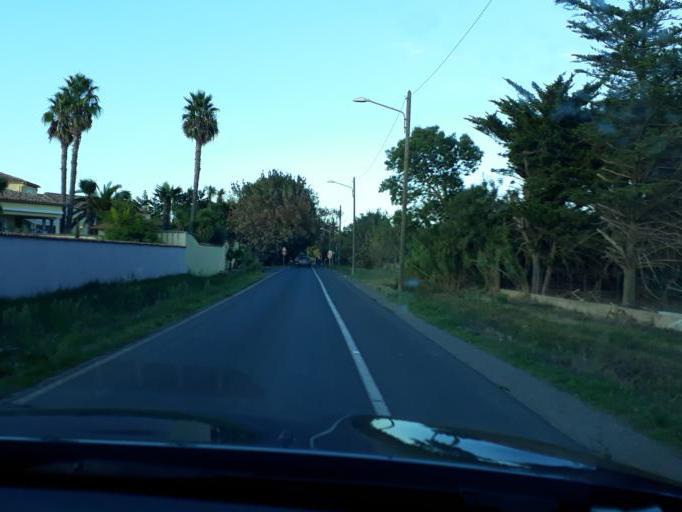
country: FR
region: Languedoc-Roussillon
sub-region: Departement de l'Herault
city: Agde
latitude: 43.2973
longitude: 3.4620
